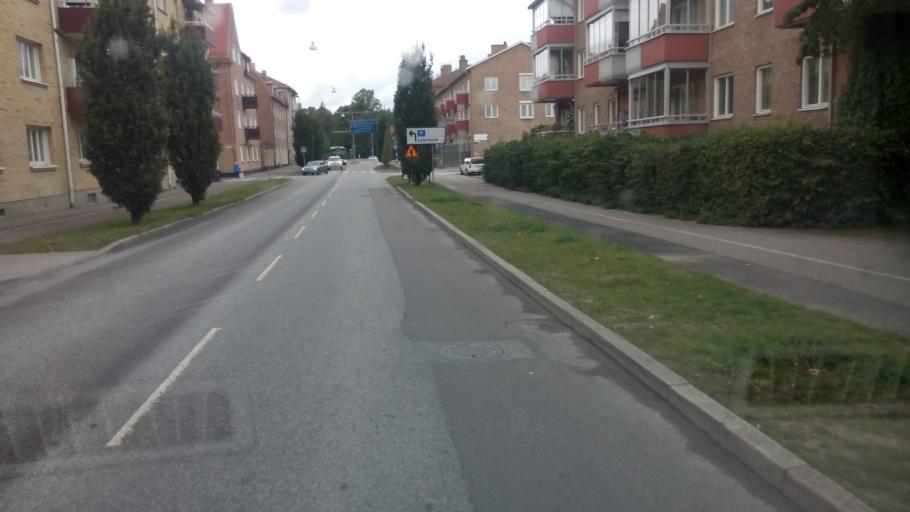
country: SE
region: Soedermanland
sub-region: Nykopings Kommun
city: Nykoping
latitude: 58.7558
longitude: 17.0179
